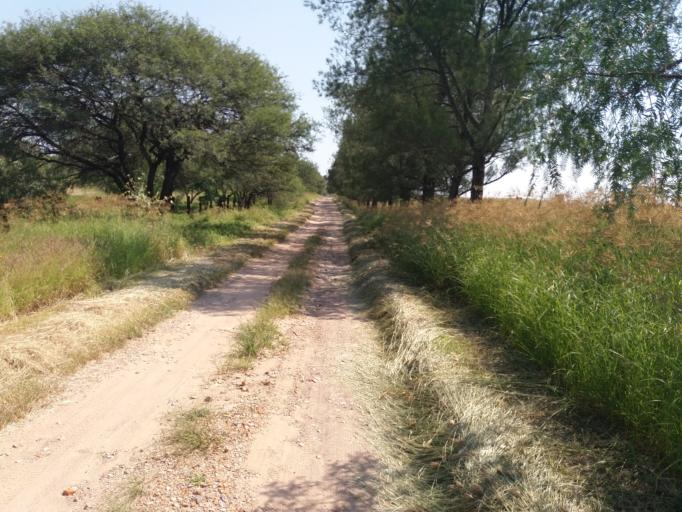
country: MX
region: Aguascalientes
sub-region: Aguascalientes
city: Penuelas (El Cienegal)
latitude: 21.7579
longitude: -102.2651
